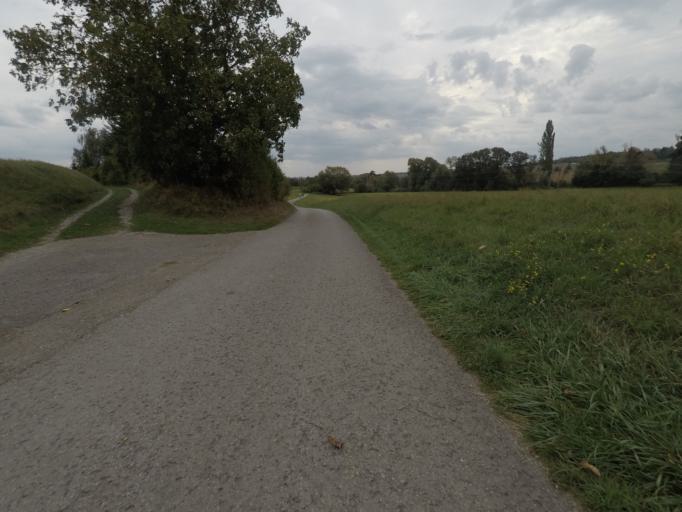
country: DE
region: Baden-Wuerttemberg
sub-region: Regierungsbezirk Stuttgart
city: Herrenberg
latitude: 48.5818
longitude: 8.8674
